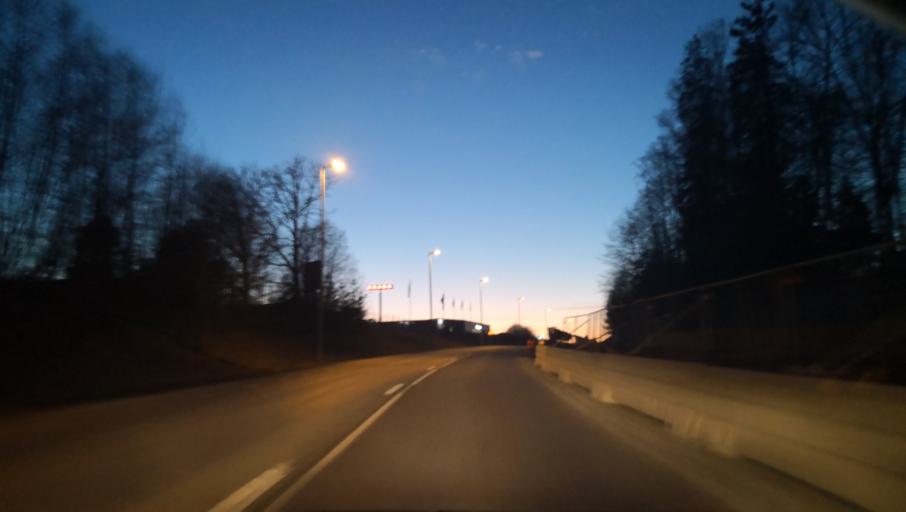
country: SE
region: Stockholm
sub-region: Nynashamns Kommun
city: Nynashamn
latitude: 58.9239
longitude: 17.9401
